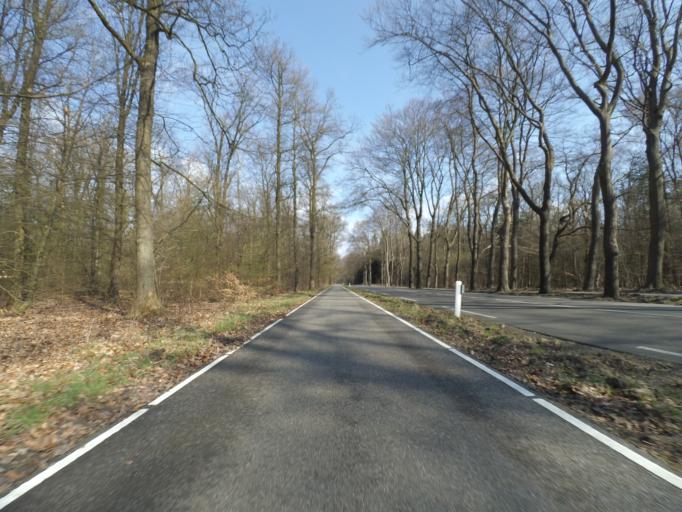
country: NL
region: Gelderland
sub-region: Gemeente Apeldoorn
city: Beekbergen
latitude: 52.1407
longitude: 5.8862
